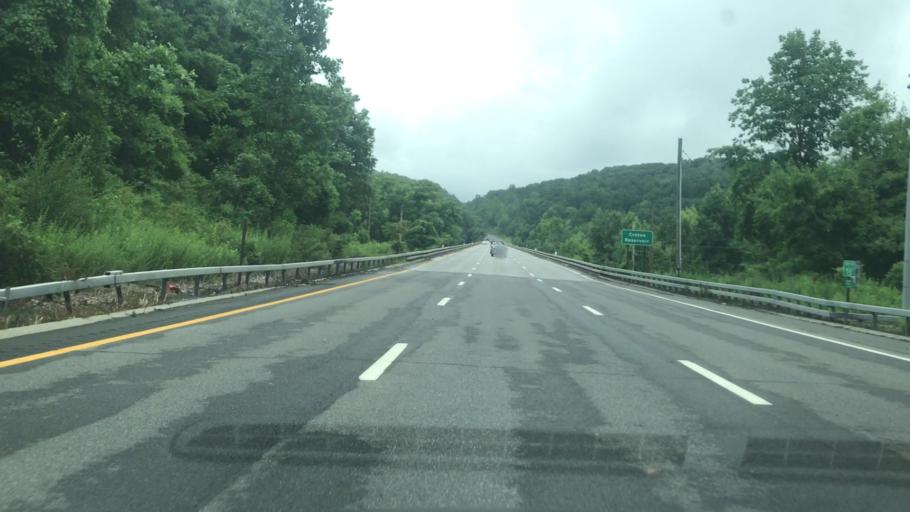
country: US
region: New York
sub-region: Westchester County
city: Yorktown Heights
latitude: 41.2417
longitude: -73.8170
